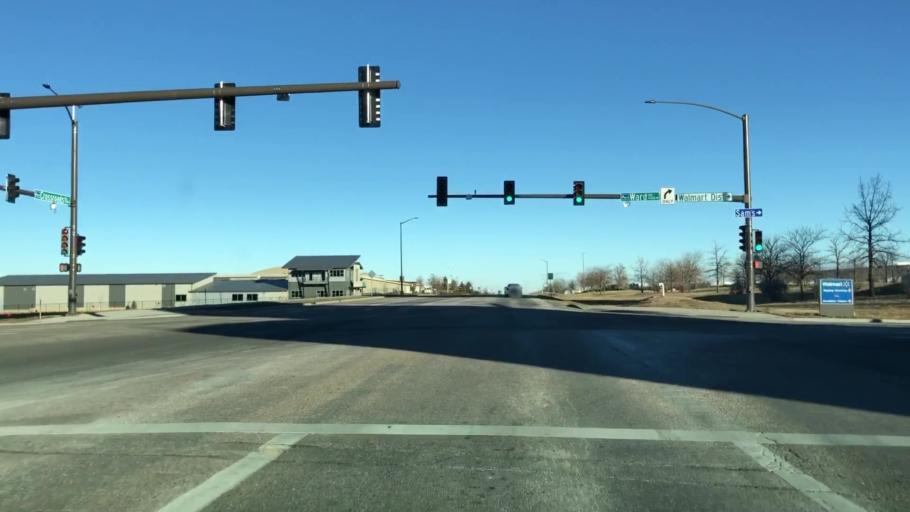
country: US
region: Colorado
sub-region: Weld County
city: Windsor
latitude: 40.4359
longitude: -104.9736
